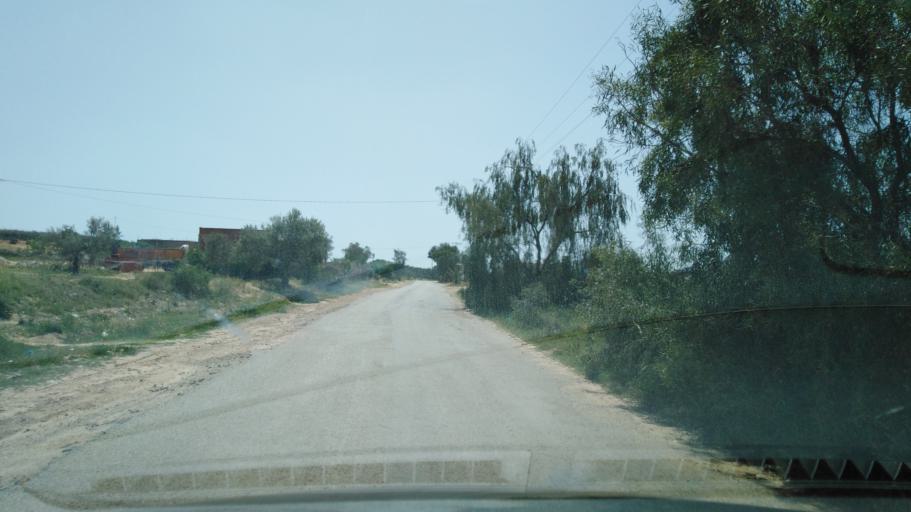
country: TN
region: Safaqis
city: Sfax
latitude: 34.7211
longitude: 10.5308
